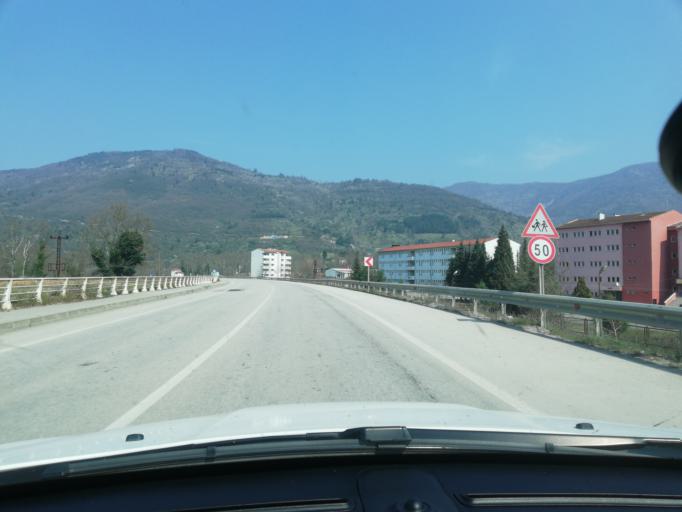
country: TR
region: Karabuk
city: Yenice
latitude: 41.2130
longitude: 32.3094
